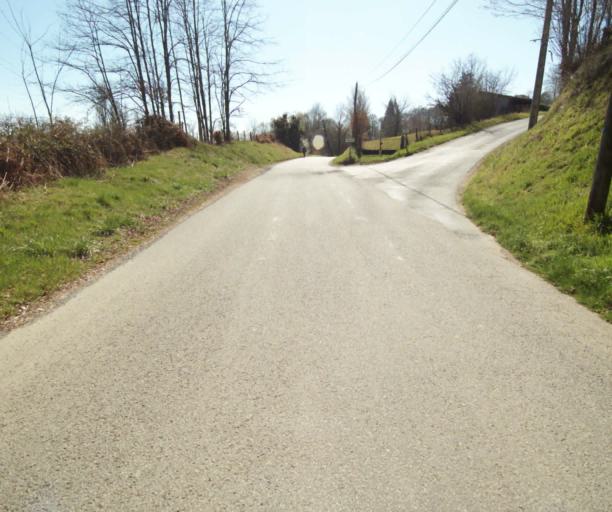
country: FR
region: Limousin
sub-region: Departement de la Correze
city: Tulle
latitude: 45.2593
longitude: 1.7326
